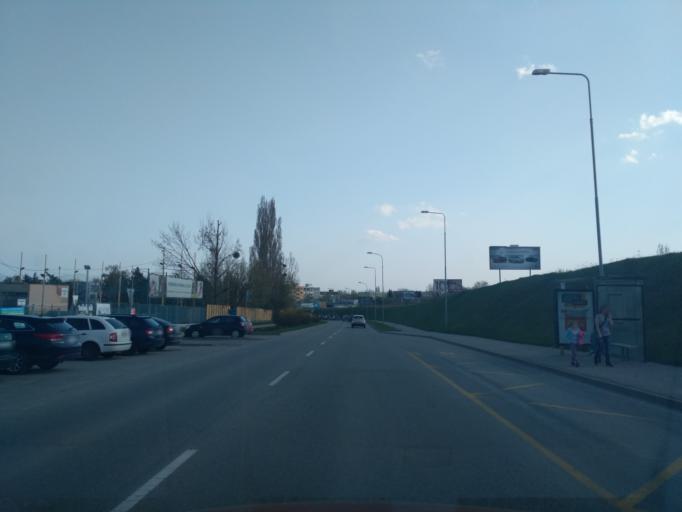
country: SK
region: Kosicky
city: Kosice
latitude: 48.7050
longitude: 21.2303
